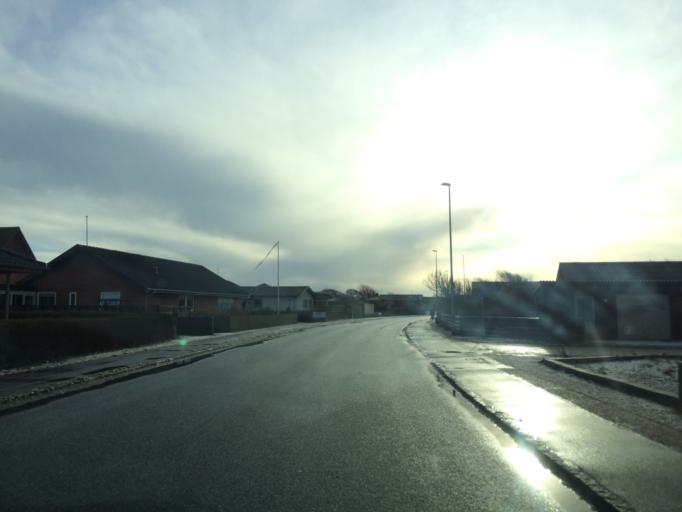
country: DK
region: Central Jutland
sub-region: Ringkobing-Skjern Kommune
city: Hvide Sande
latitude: 56.0131
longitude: 8.1271
